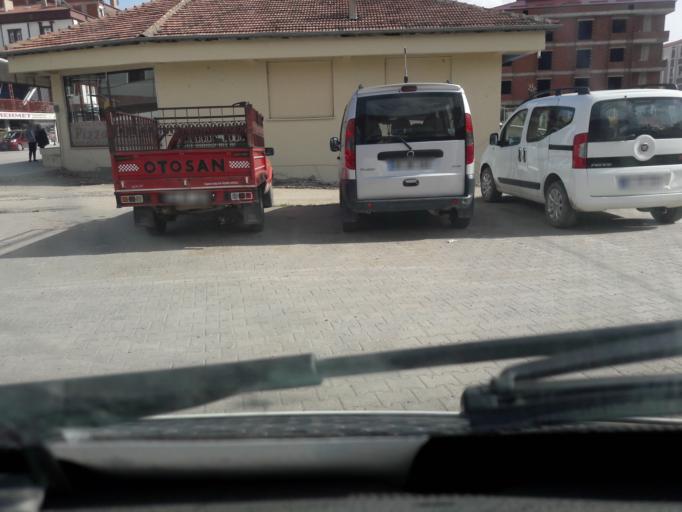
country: TR
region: Gumushane
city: Kelkit
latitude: 40.1337
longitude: 39.4355
